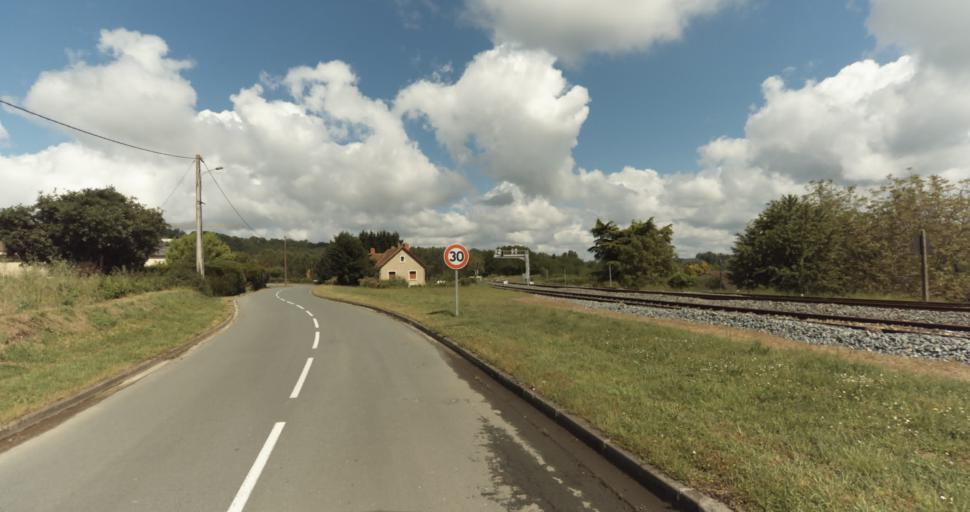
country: FR
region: Aquitaine
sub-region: Departement de la Dordogne
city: Le Bugue
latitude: 44.8489
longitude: 0.9014
